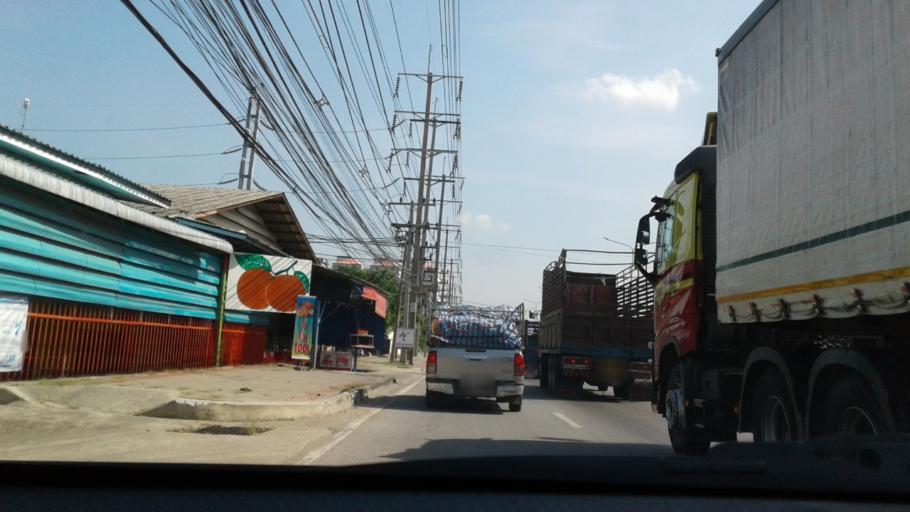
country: TH
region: Phra Nakhon Si Ayutthaya
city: Ban Bang Kadi Pathum Thani
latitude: 13.9771
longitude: 100.5859
